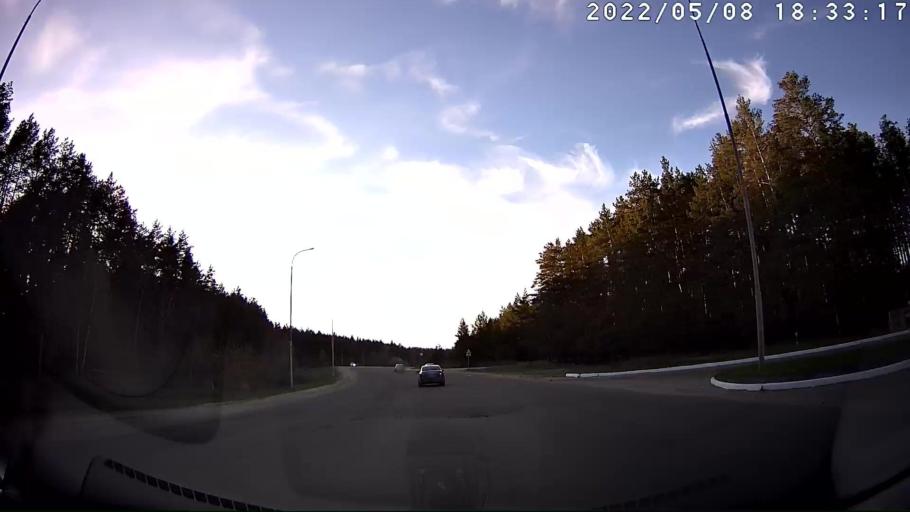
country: RU
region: Mariy-El
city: Volzhsk
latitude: 55.8896
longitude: 48.3584
